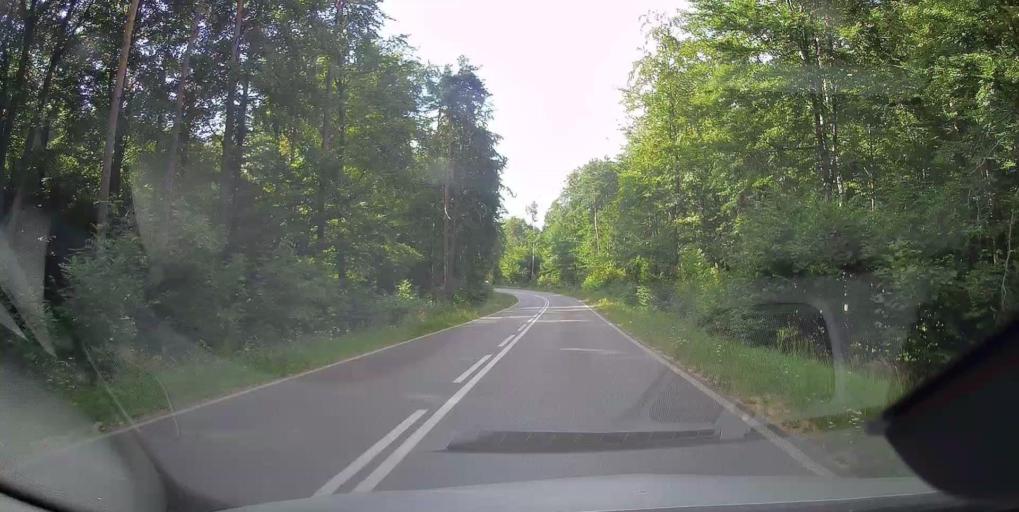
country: PL
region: Swietokrzyskie
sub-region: Powiat skarzyski
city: Suchedniow
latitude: 50.9918
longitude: 20.8610
